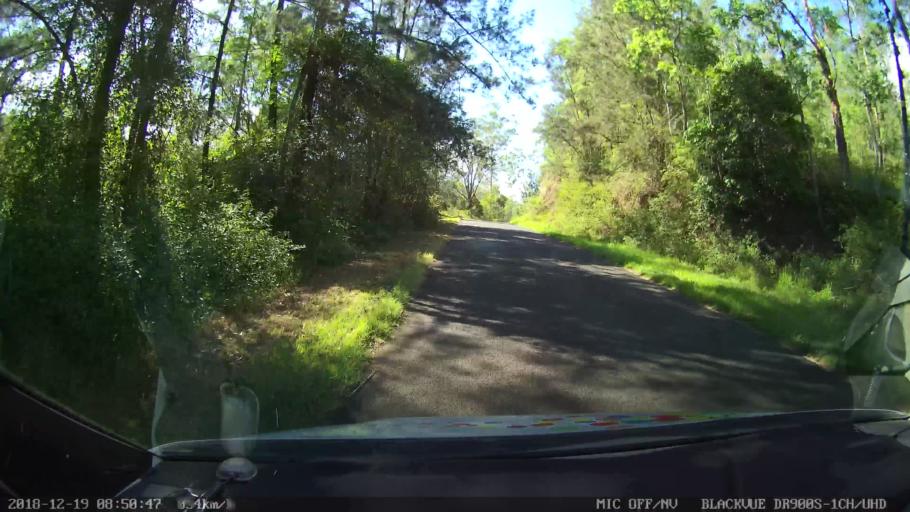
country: AU
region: New South Wales
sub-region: Kyogle
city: Kyogle
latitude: -28.3834
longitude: 152.9762
